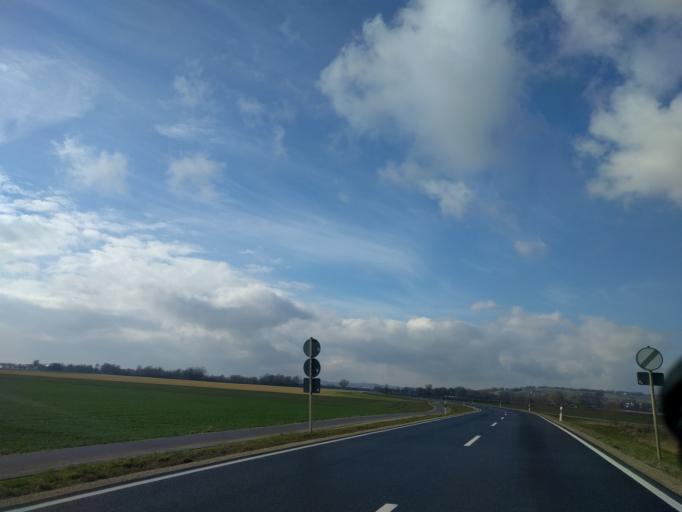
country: DE
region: Bavaria
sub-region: Swabia
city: Asbach-Baumenheim
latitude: 48.7103
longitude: 10.8420
